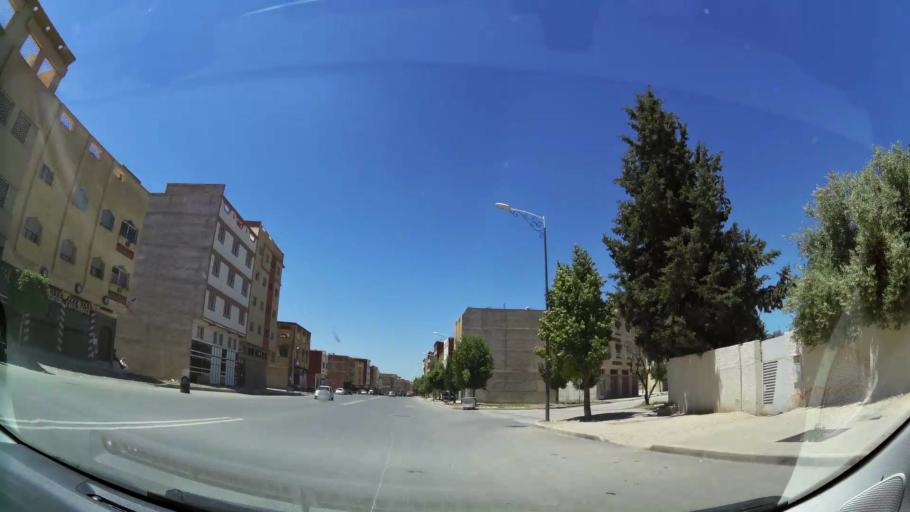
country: MA
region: Oriental
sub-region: Oujda-Angad
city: Oujda
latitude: 34.6757
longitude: -1.8692
